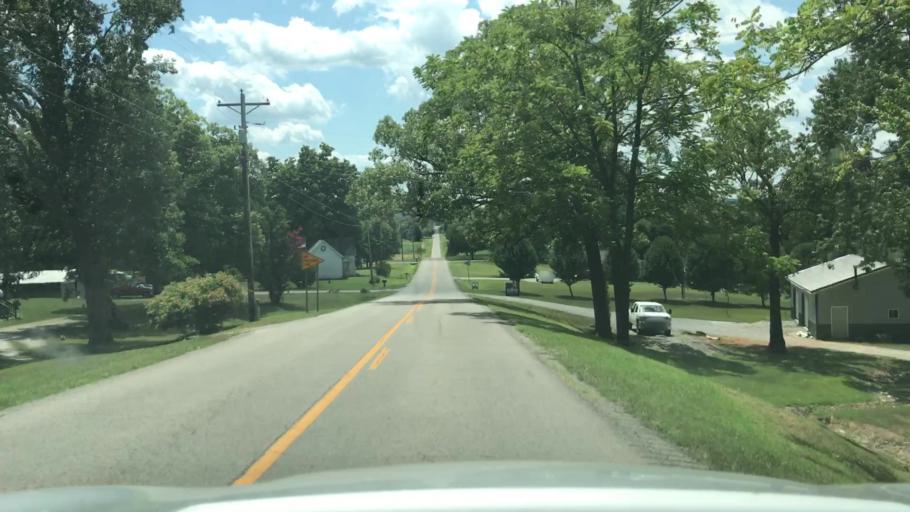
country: US
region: Kentucky
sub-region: Muhlenberg County
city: Greenville
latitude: 37.1628
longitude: -87.2501
